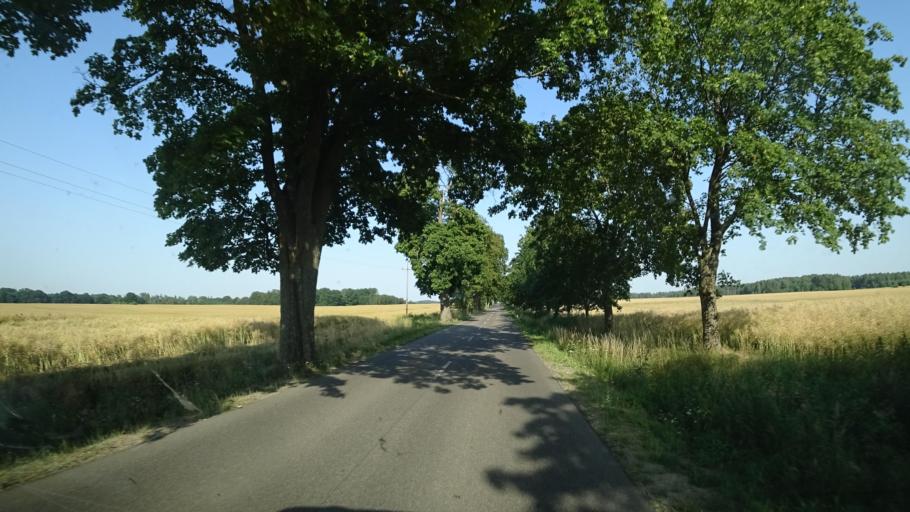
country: PL
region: Pomeranian Voivodeship
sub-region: Powiat czluchowski
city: Przechlewo
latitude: 53.8042
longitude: 17.2938
